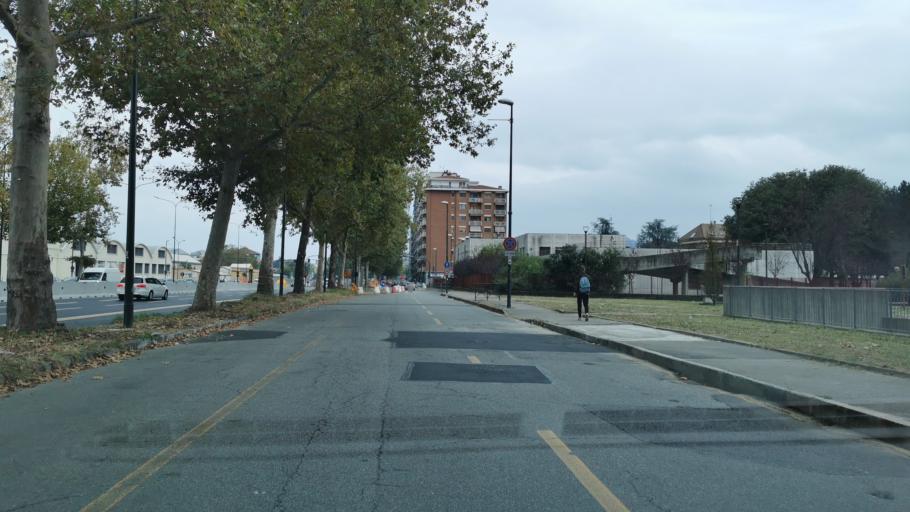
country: IT
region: Piedmont
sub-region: Provincia di Torino
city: Turin
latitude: 45.1040
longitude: 7.6826
